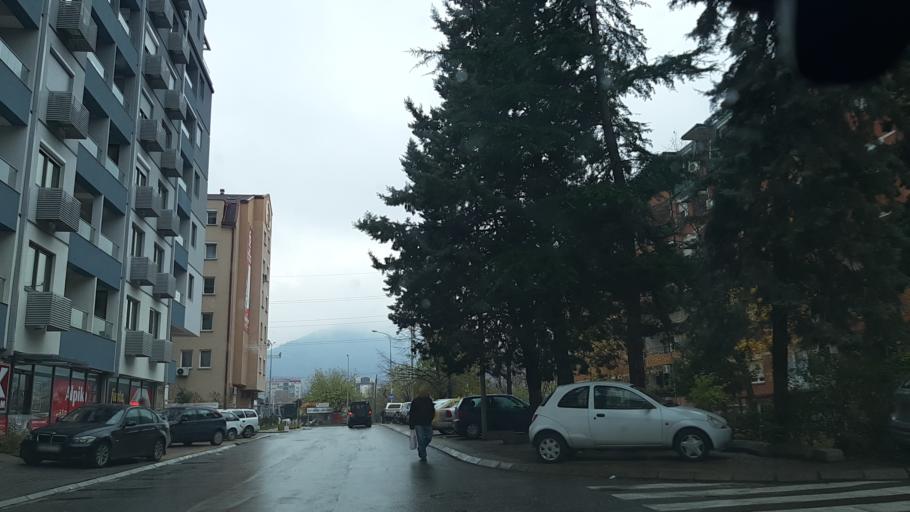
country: MK
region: Karpos
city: Skopje
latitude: 41.9859
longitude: 21.4487
